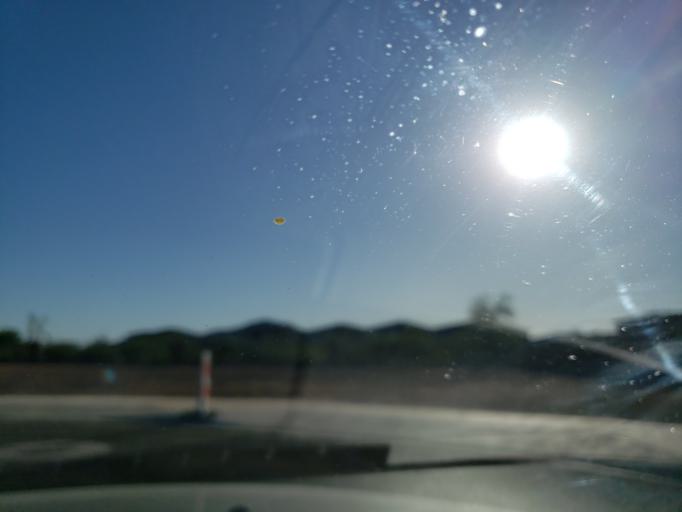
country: US
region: Arizona
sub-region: Maricopa County
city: Cave Creek
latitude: 33.6854
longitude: -112.0161
